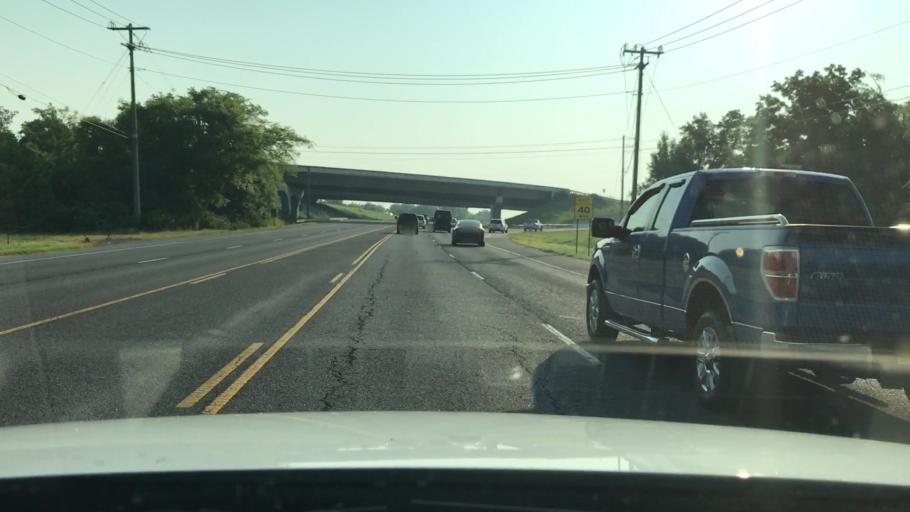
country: US
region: Tennessee
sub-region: Sumner County
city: Hendersonville
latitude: 36.3275
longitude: -86.5608
